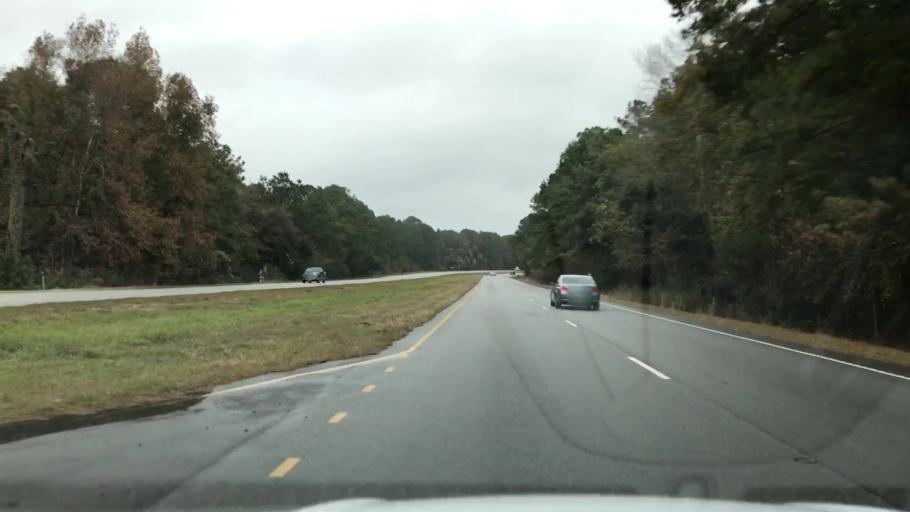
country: US
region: South Carolina
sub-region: Charleston County
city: Awendaw
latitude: 32.9330
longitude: -79.7128
